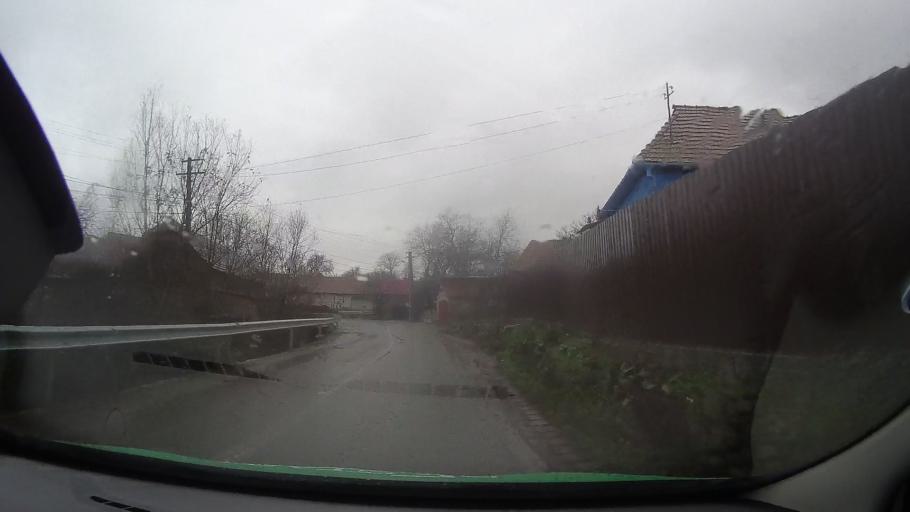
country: RO
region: Mures
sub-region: Comuna Vatava
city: Vatava
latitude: 46.9603
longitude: 24.7608
